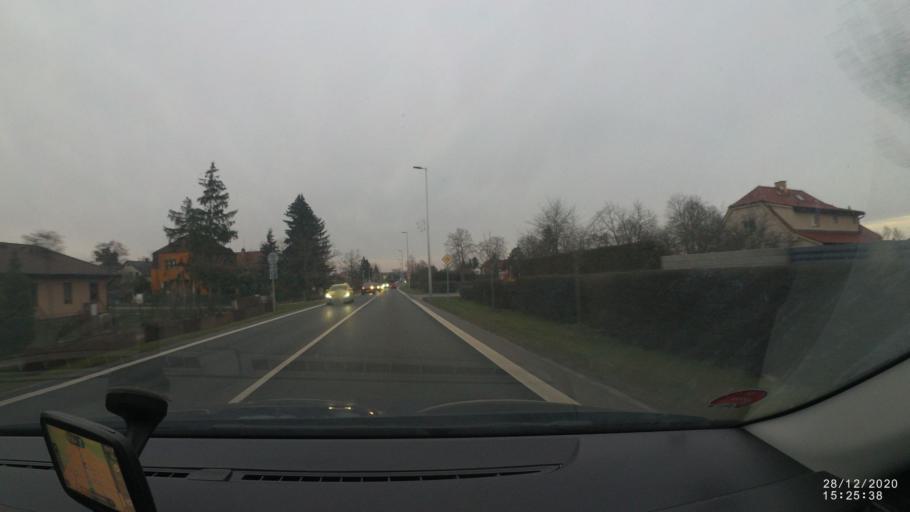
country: CZ
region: Praha
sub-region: Praha 20
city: Horni Pocernice
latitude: 50.0801
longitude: 14.6230
